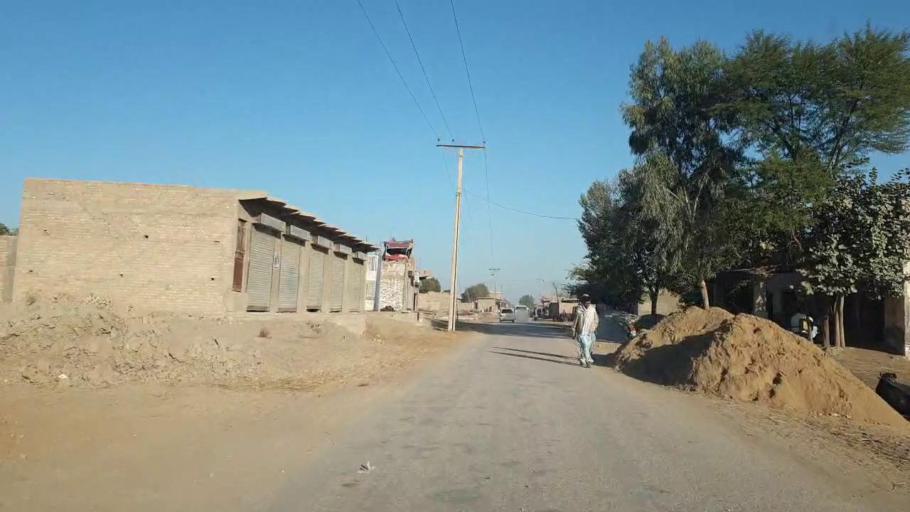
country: PK
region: Sindh
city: Dokri
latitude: 27.3672
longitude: 68.0983
